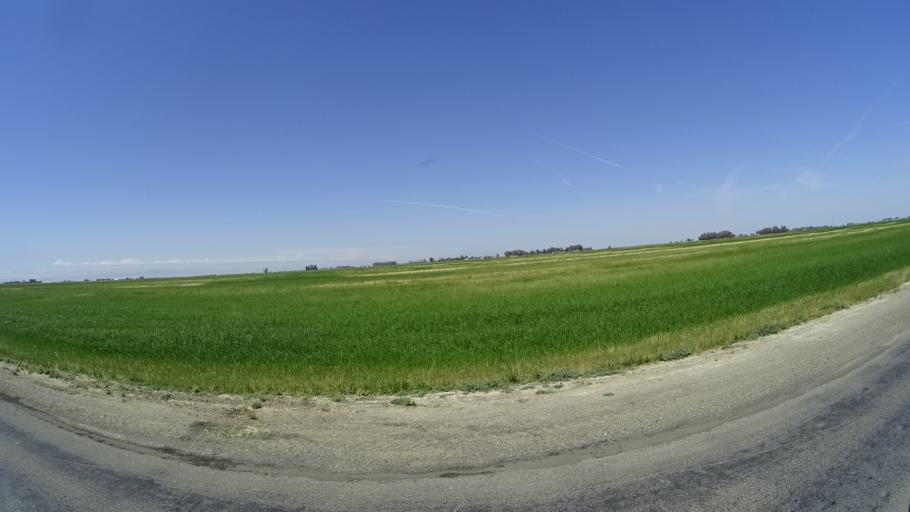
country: US
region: California
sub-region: Kings County
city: Stratford
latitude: 36.1934
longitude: -119.7624
